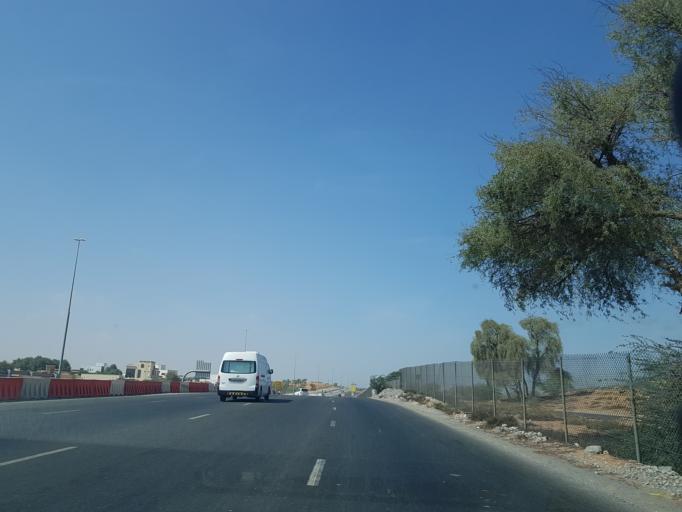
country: AE
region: Ra's al Khaymah
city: Ras al-Khaimah
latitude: 25.7016
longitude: 55.9640
